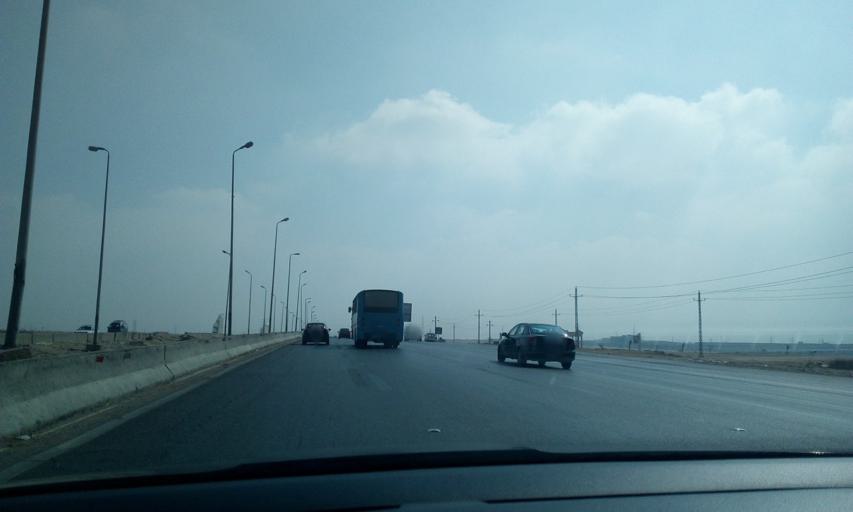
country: EG
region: Eastern Province
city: Bilbays
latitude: 30.2296
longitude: 31.7038
